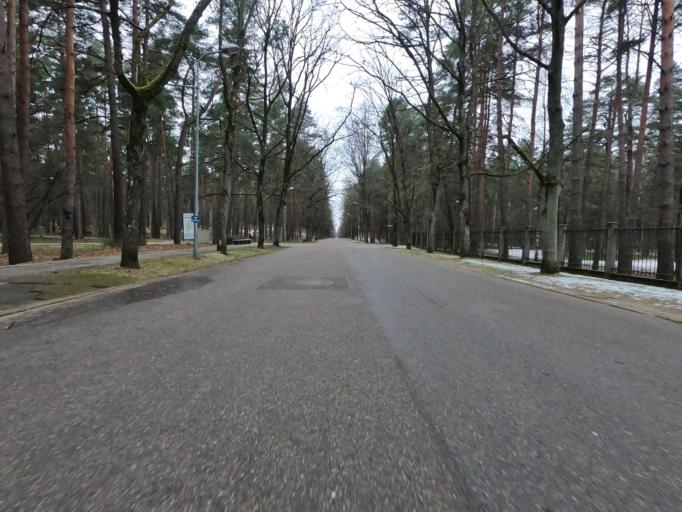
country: LV
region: Riga
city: Jaunciems
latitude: 57.0143
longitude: 24.1499
